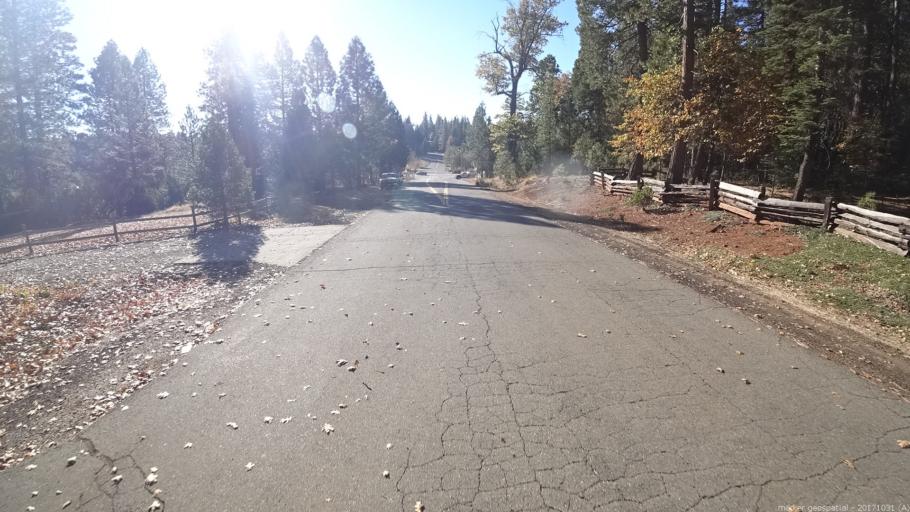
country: US
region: California
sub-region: Shasta County
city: Shingletown
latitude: 40.4937
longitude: -121.8875
